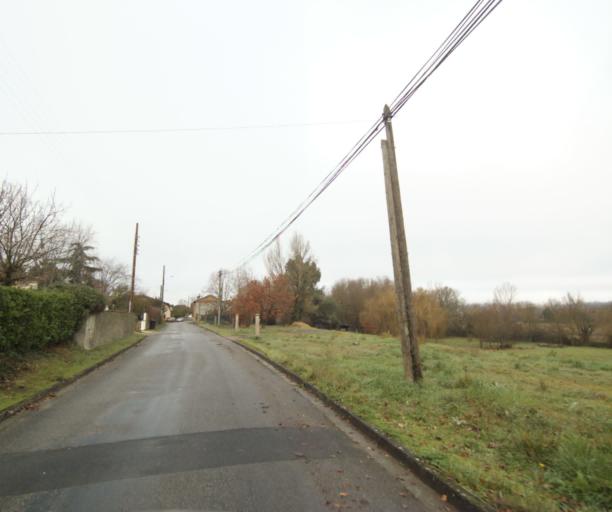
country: FR
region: Midi-Pyrenees
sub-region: Departement du Tarn-et-Garonne
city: Nohic
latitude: 43.8734
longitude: 1.4666
